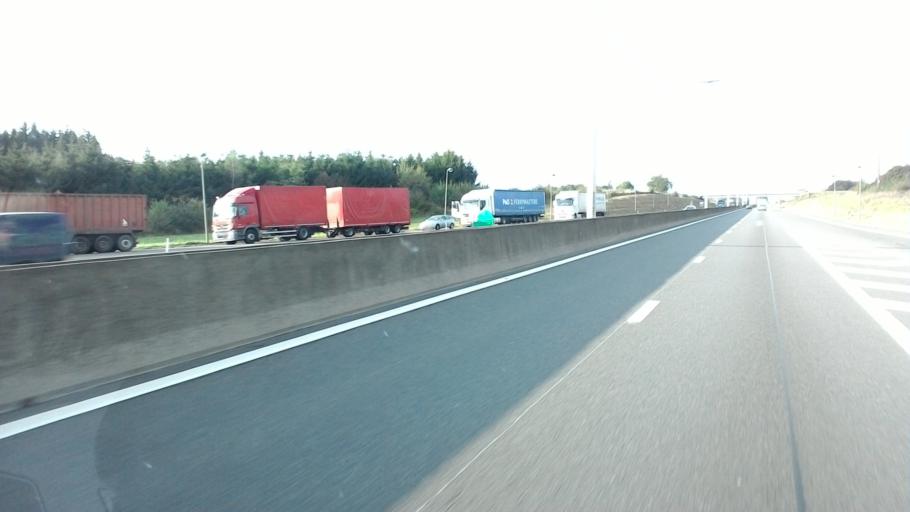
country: BE
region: Wallonia
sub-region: Province du Luxembourg
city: Leglise
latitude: 49.8291
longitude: 5.5131
